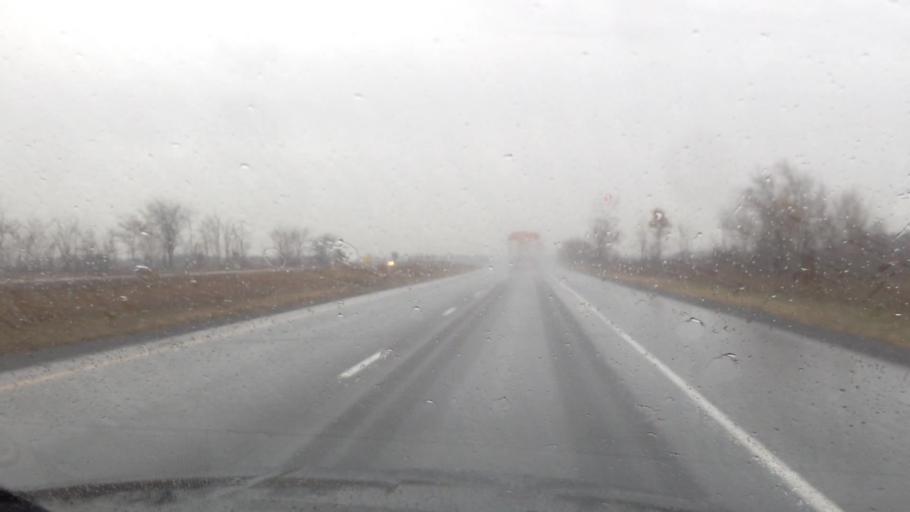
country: CA
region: Ontario
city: Casselman
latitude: 45.3297
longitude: -74.9447
